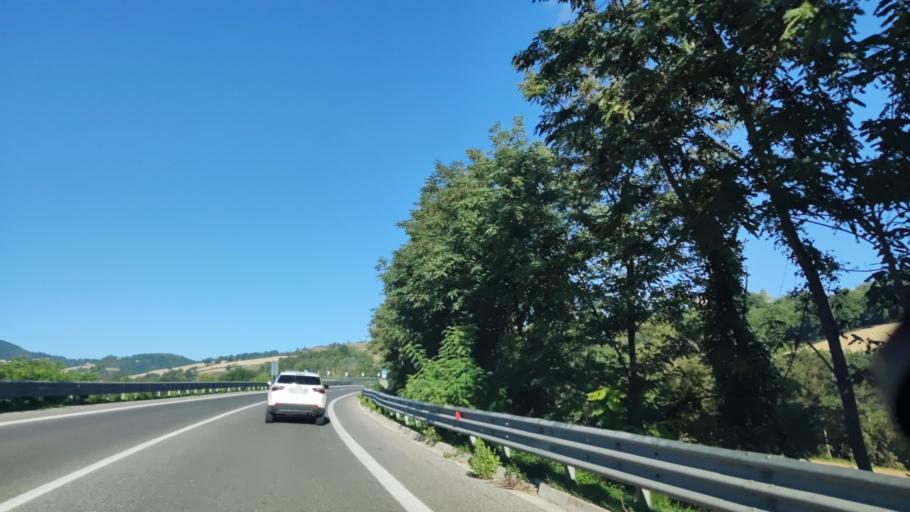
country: IT
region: The Marches
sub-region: Provincia di Pesaro e Urbino
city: Fermignano
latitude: 43.7060
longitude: 12.6457
